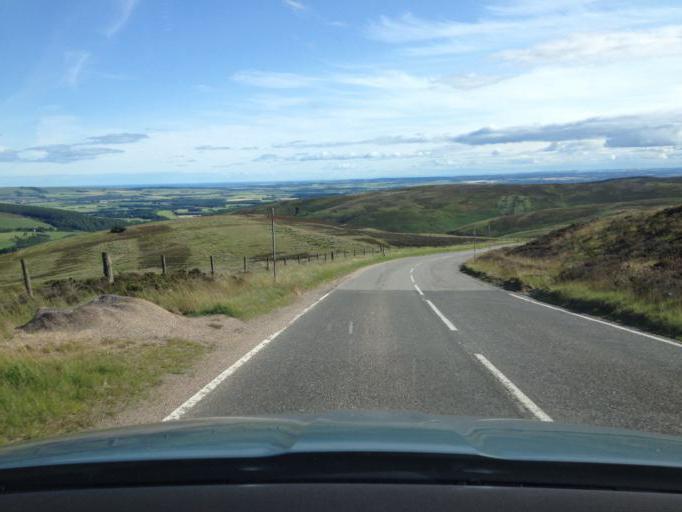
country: GB
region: Scotland
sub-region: Aberdeenshire
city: Laurencekirk
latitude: 56.9135
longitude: -2.5723
